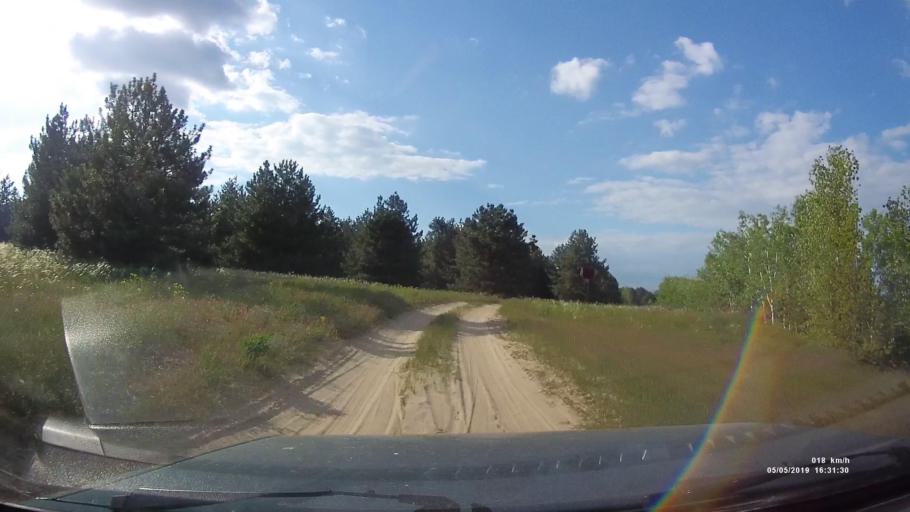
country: RU
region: Rostov
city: Ust'-Donetskiy
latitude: 47.7764
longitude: 41.0147
